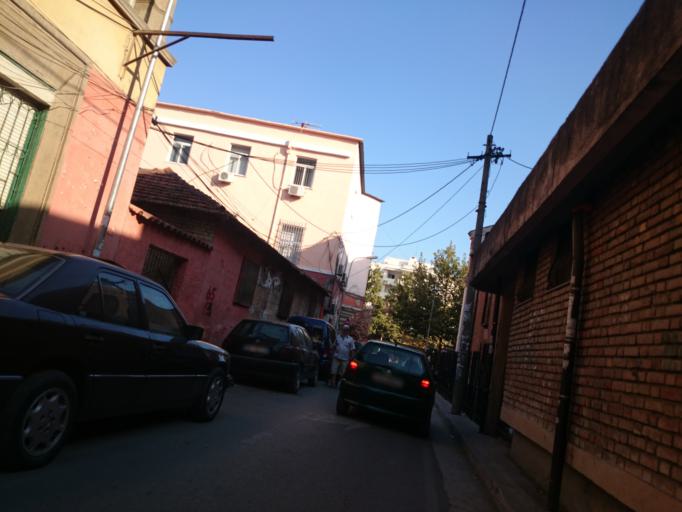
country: AL
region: Tirane
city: Tirana
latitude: 41.3270
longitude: 19.8094
